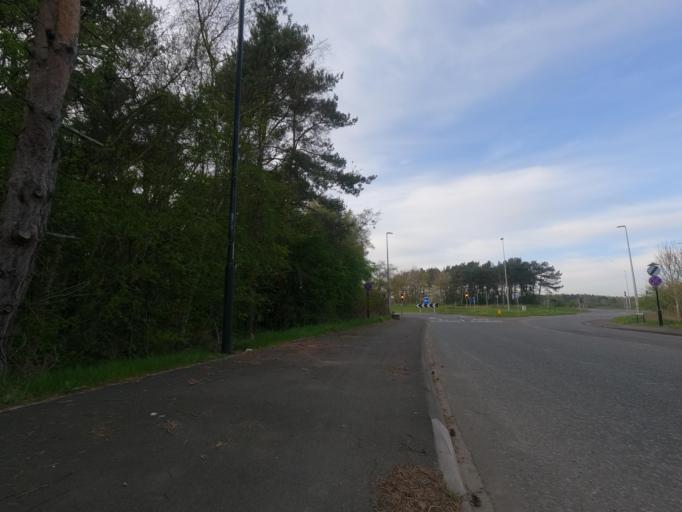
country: GB
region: England
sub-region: Newcastle upon Tyne
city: Hazlerigg
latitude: 55.0641
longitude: -1.6327
